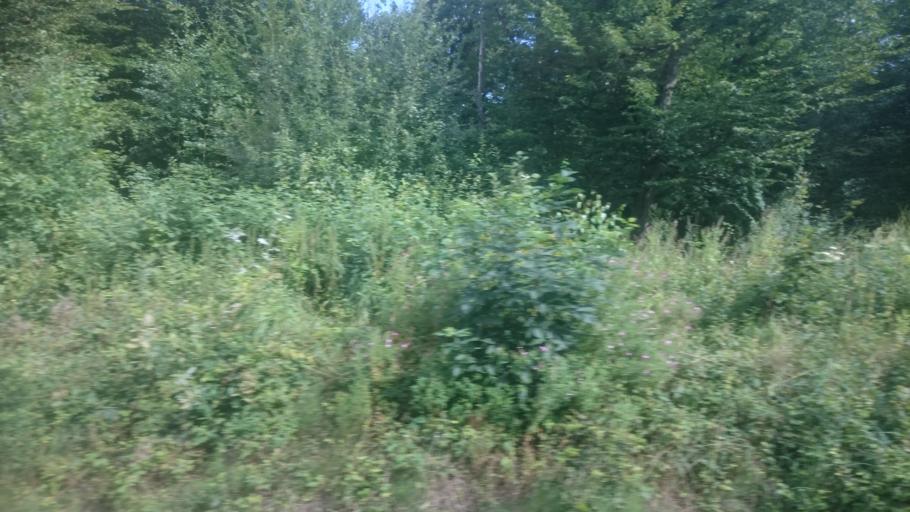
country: RU
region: Kaliningrad
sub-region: Gorod Kaliningrad
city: Pionerskiy
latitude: 54.9508
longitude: 20.2201
